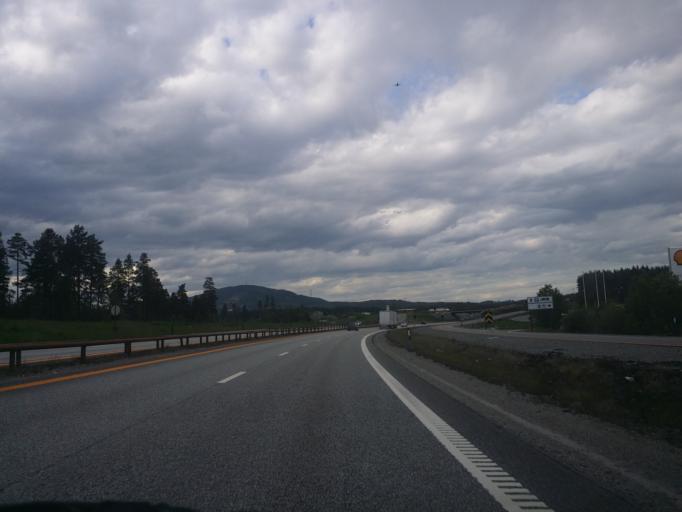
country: NO
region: Akershus
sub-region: Eidsvoll
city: Raholt
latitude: 60.3104
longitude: 11.1419
